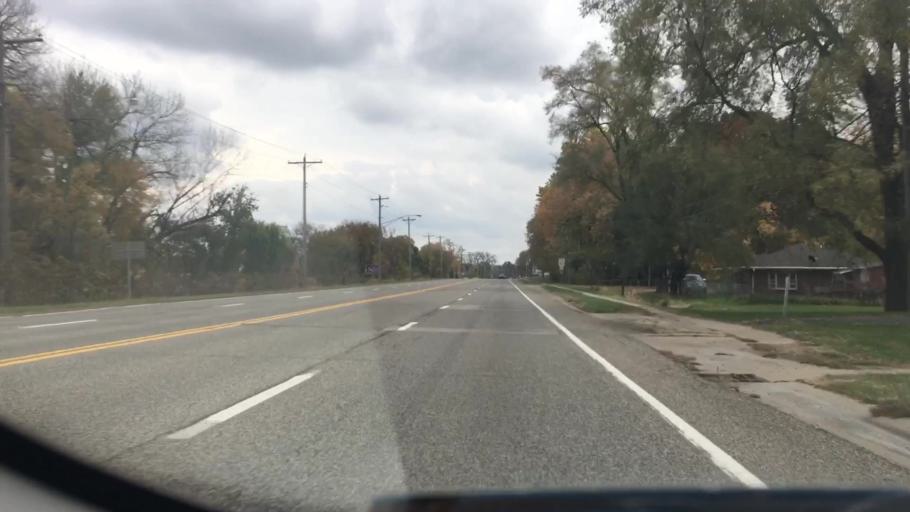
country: US
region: Illinois
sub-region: Peoria County
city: Peoria Heights
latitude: 40.7509
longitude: -89.5601
